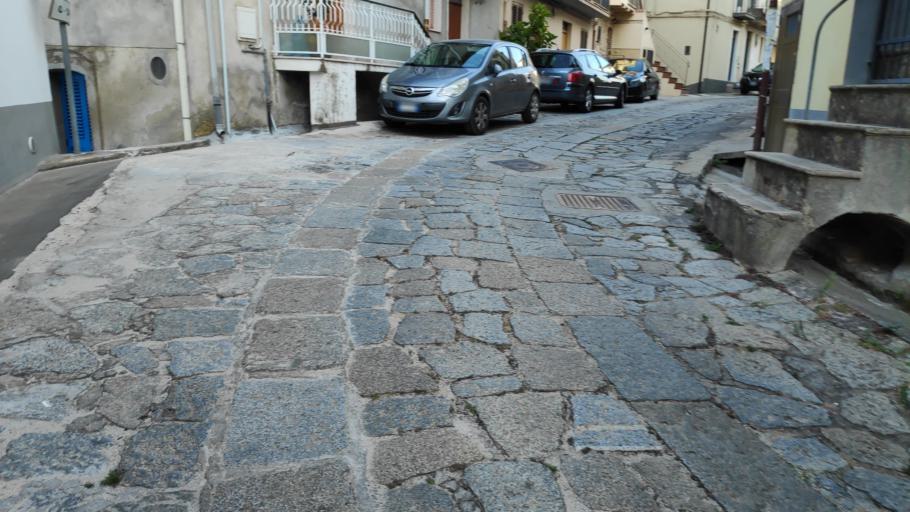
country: IT
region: Calabria
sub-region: Provincia di Catanzaro
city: Sant'Andrea Apostolo dello Ionio
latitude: 38.6208
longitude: 16.5315
